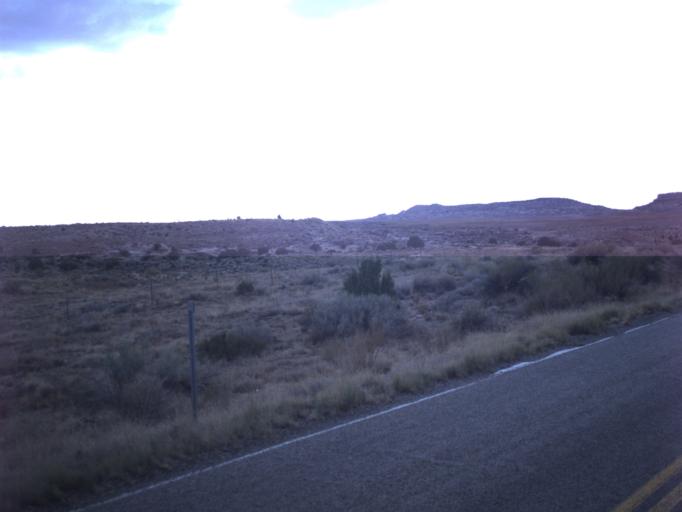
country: US
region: Utah
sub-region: San Juan County
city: Blanding
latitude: 37.4193
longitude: -109.4357
